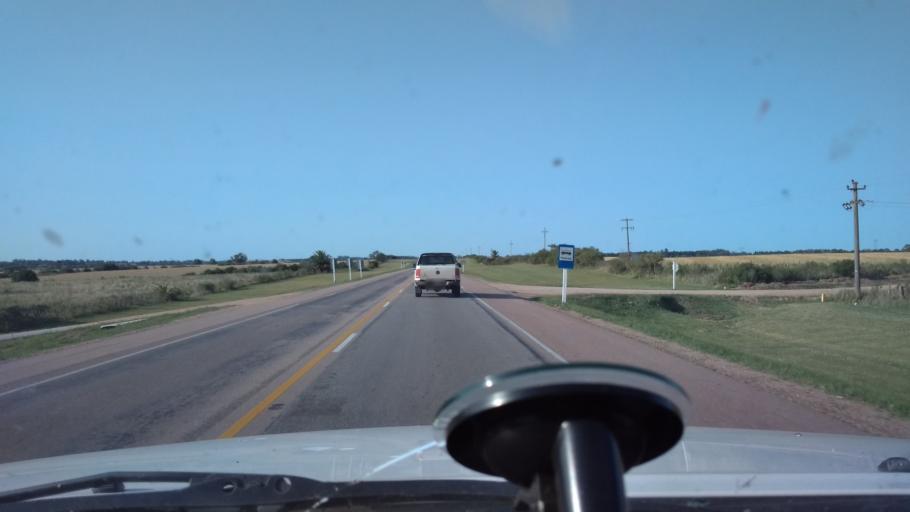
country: UY
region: Canelones
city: Canelones
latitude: -34.4853
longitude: -56.2819
